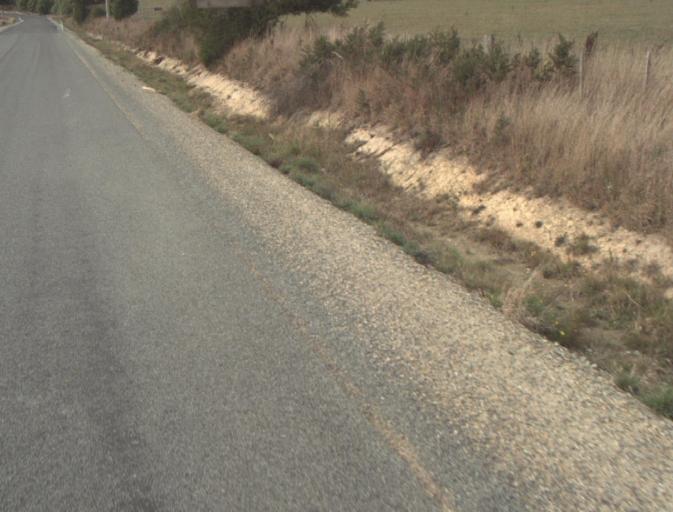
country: AU
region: Tasmania
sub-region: Launceston
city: Mayfield
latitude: -41.2034
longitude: 147.1890
